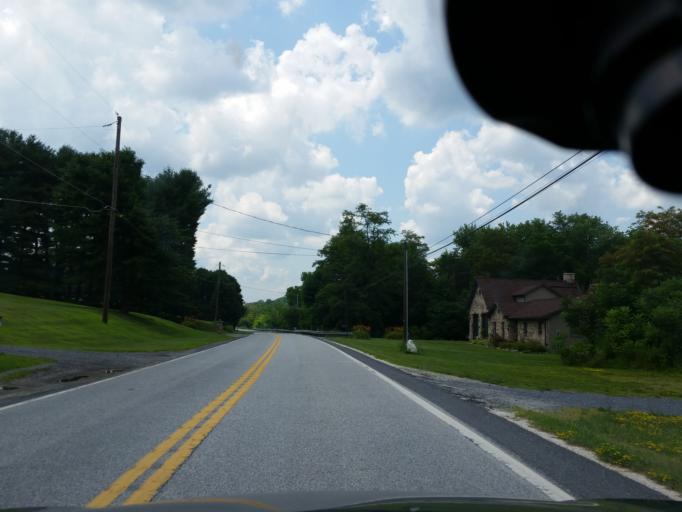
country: US
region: Pennsylvania
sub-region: Perry County
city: Duncannon
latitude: 40.3225
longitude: -77.0977
